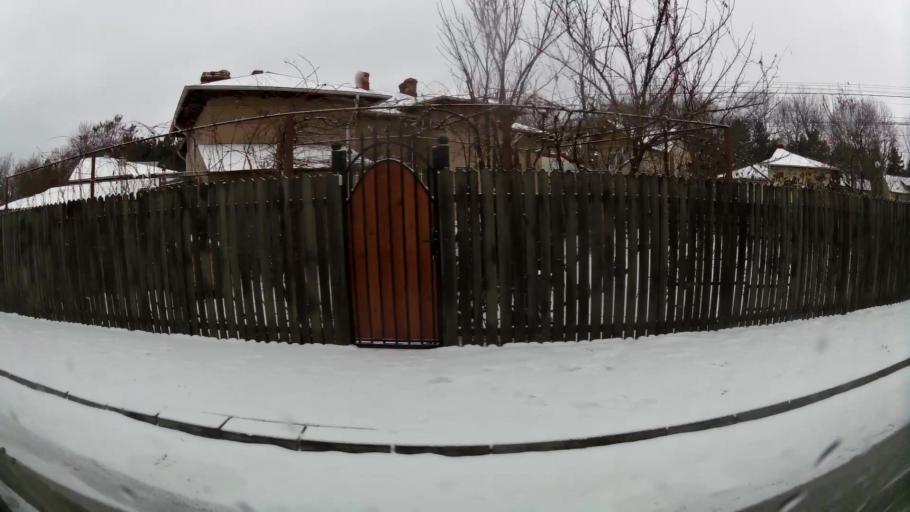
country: RO
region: Prahova
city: Ploiesti
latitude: 44.9322
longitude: 26.0155
